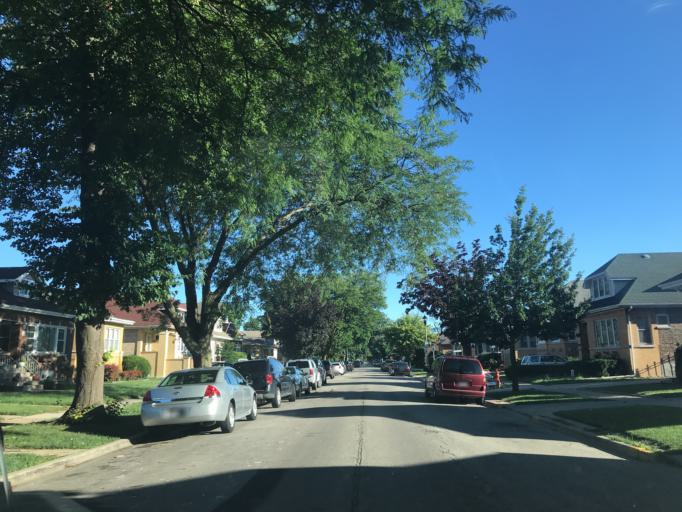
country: US
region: Illinois
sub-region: Cook County
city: Berwyn
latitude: 41.8557
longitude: -87.7874
